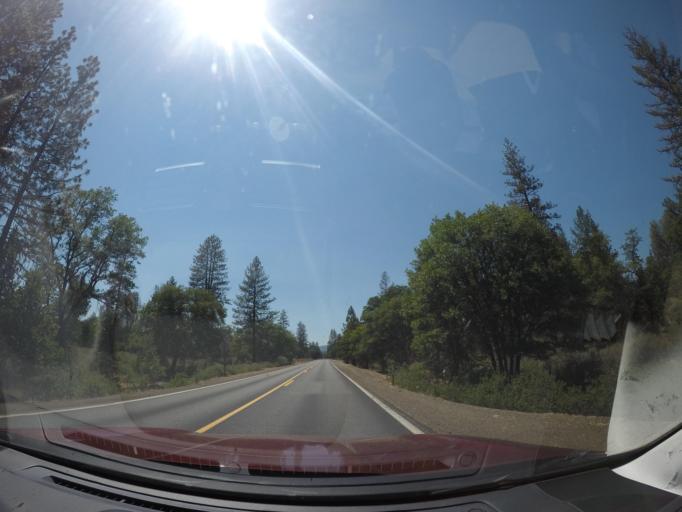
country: US
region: California
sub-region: Shasta County
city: Burney
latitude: 40.9833
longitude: -121.5258
